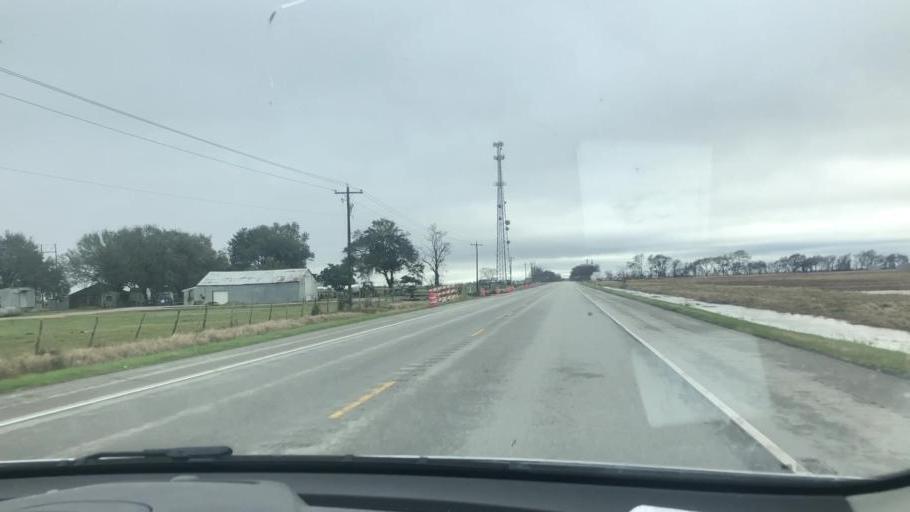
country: US
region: Texas
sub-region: Wharton County
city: Boling
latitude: 29.1405
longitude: -95.9851
